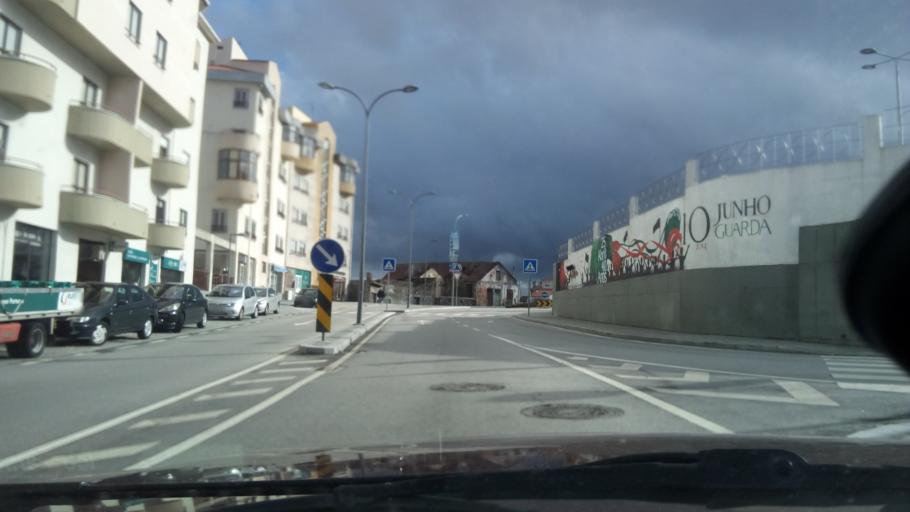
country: PT
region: Guarda
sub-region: Guarda
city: Guarda
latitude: 40.5351
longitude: -7.2631
